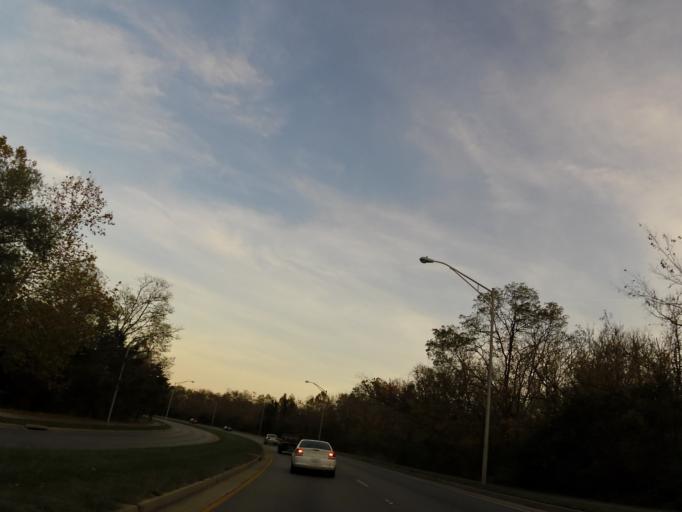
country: US
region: Kentucky
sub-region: Fayette County
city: Lexington
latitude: 37.9684
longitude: -84.5087
